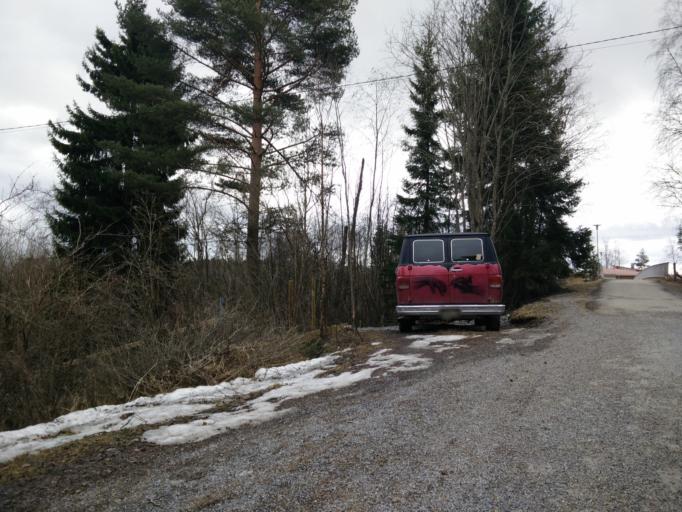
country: FI
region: Pirkanmaa
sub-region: Tampere
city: Orivesi
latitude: 61.6854
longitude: 24.3543
